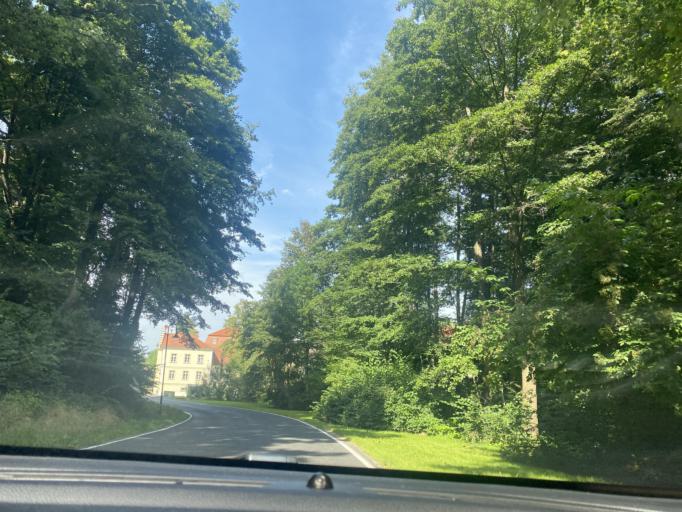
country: DE
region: Saxony
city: Sohland am Rotstein
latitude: 51.1148
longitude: 14.7827
